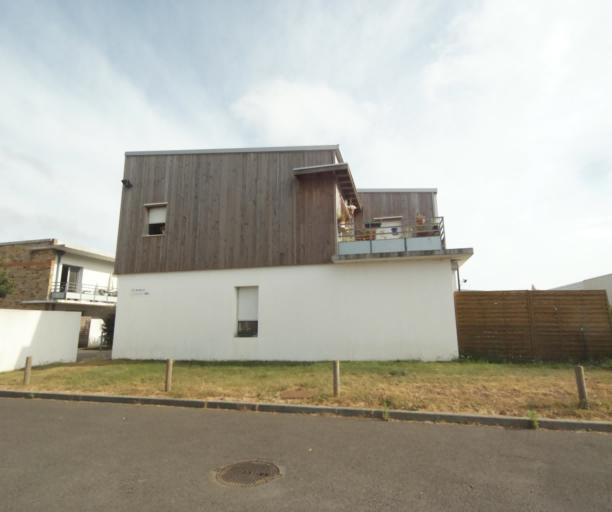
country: FR
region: Pays de la Loire
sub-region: Departement de la Vendee
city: Chateau-d'Olonne
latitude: 46.4898
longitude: -1.7353
